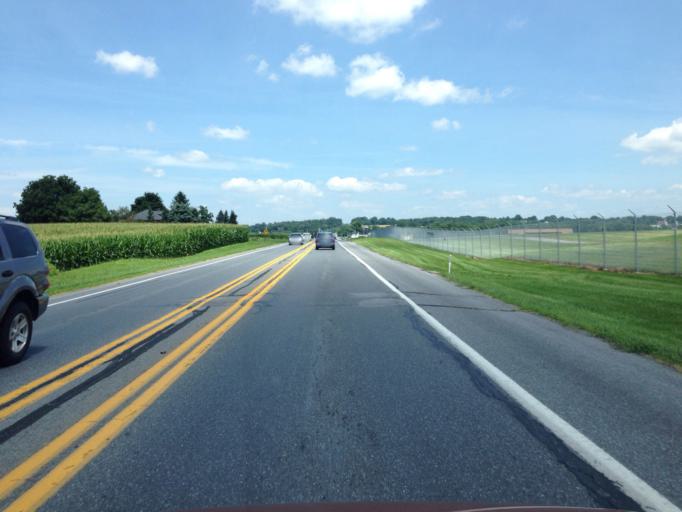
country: US
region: Pennsylvania
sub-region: Lancaster County
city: Lititz
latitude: 40.1197
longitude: -76.3057
